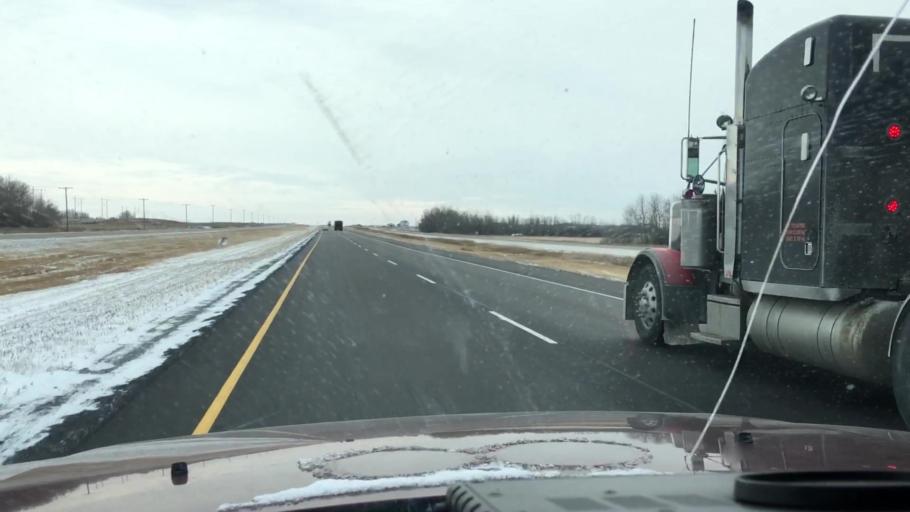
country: CA
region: Saskatchewan
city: Saskatoon
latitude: 51.9383
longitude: -106.5392
